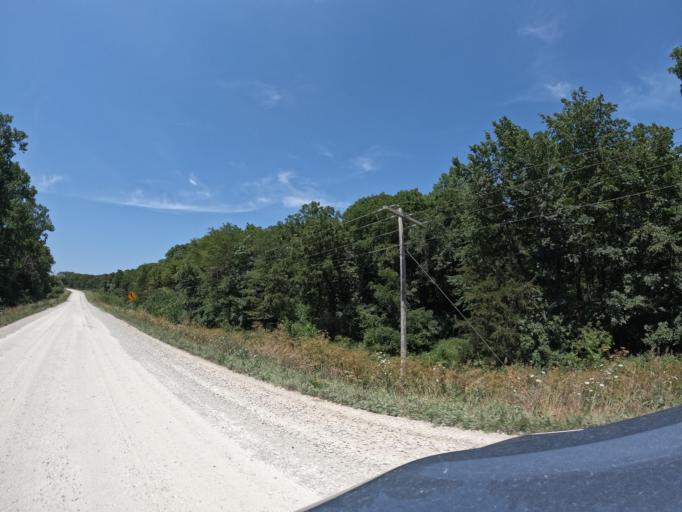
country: US
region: Iowa
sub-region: Henry County
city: Mount Pleasant
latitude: 40.9271
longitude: -91.6326
